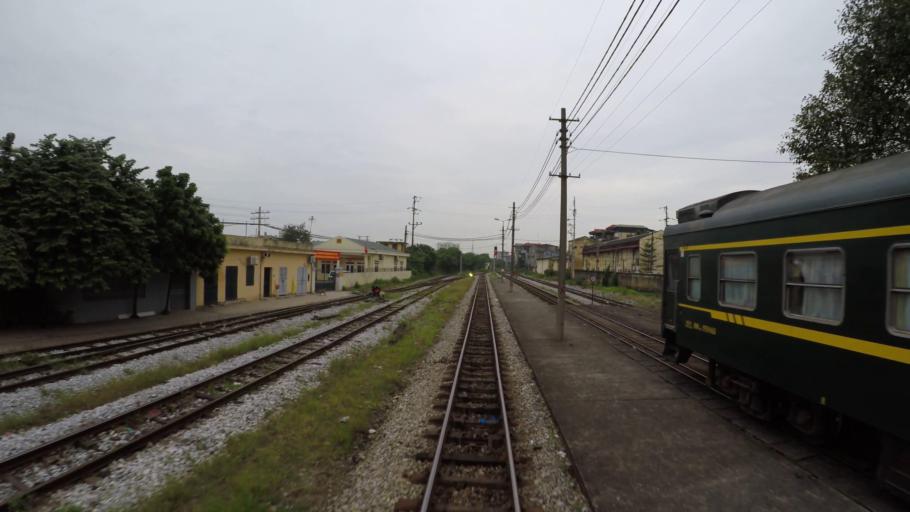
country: VN
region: Ha Noi
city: Trau Quy
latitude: 21.0250
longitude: 105.9272
